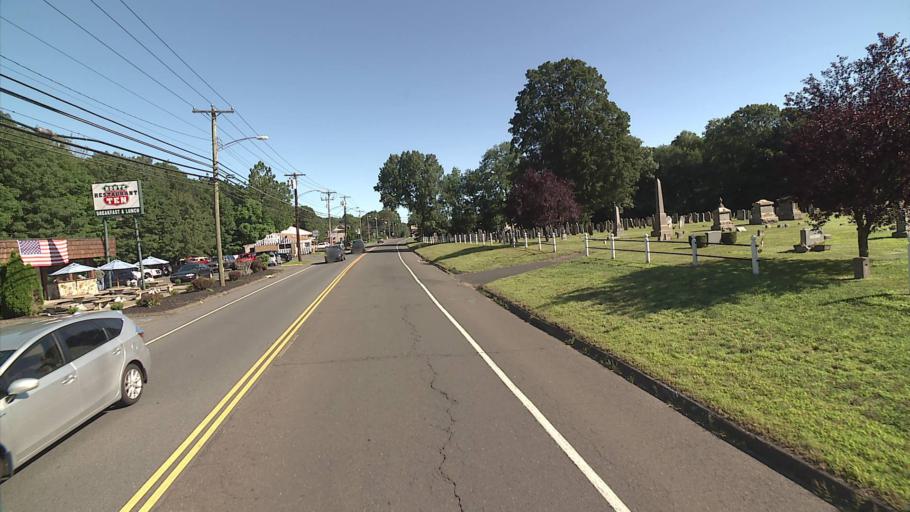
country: US
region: Connecticut
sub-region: New Haven County
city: Hamden
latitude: 41.4315
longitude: -72.9075
